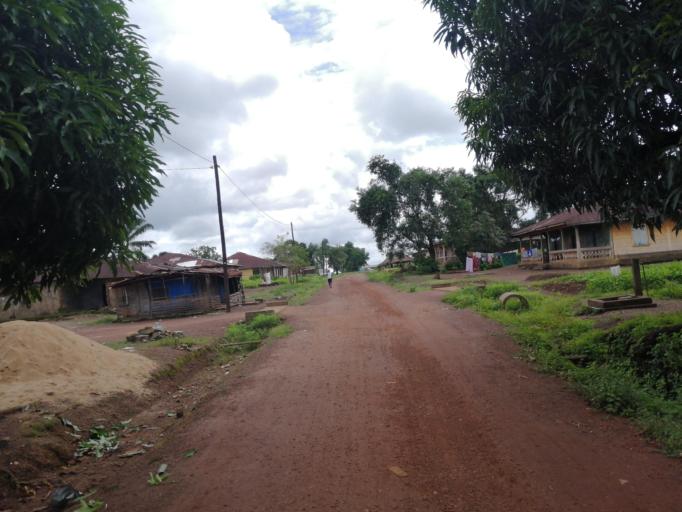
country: SL
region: Northern Province
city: Port Loko
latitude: 8.7732
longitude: -12.7903
